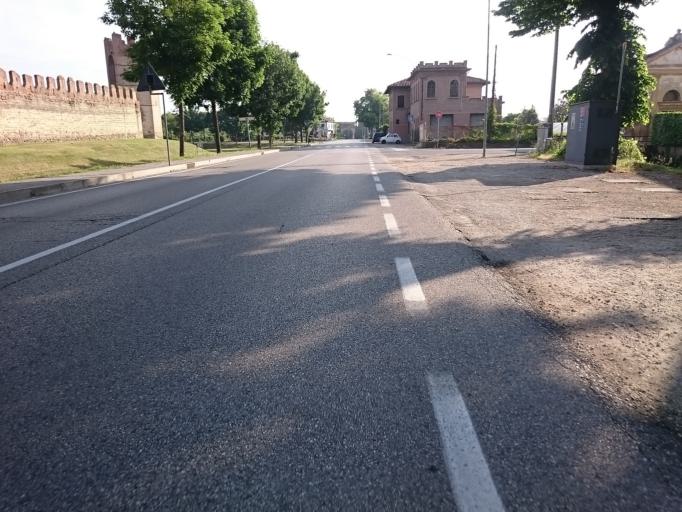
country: IT
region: Veneto
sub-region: Provincia di Padova
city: Montagnana
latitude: 45.2314
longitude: 11.4703
